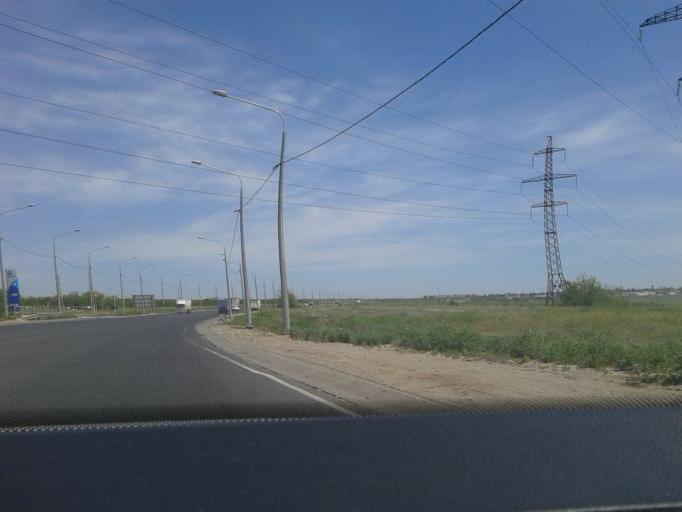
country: RU
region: Volgograd
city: Vodstroy
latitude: 48.8236
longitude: 44.5263
